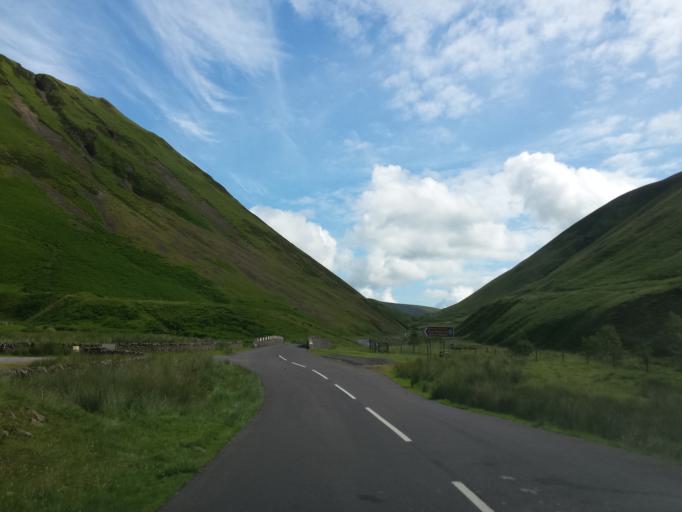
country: GB
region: Scotland
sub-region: Dumfries and Galloway
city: Moffat
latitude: 55.4172
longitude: -3.2872
